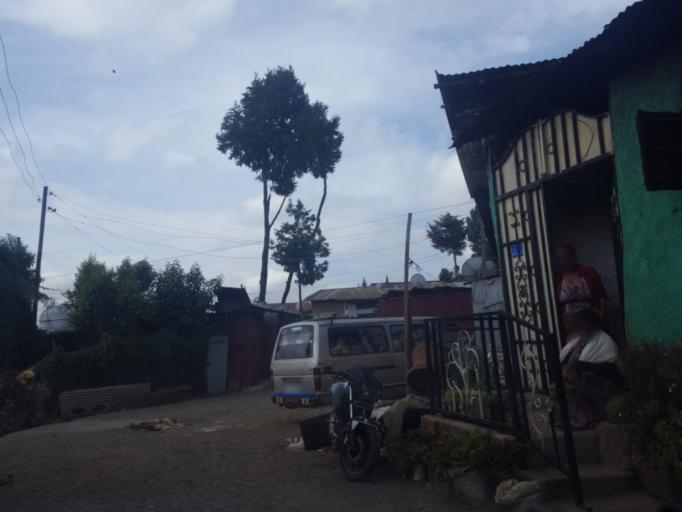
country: ET
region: Adis Abeba
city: Addis Ababa
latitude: 9.0654
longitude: 38.7470
